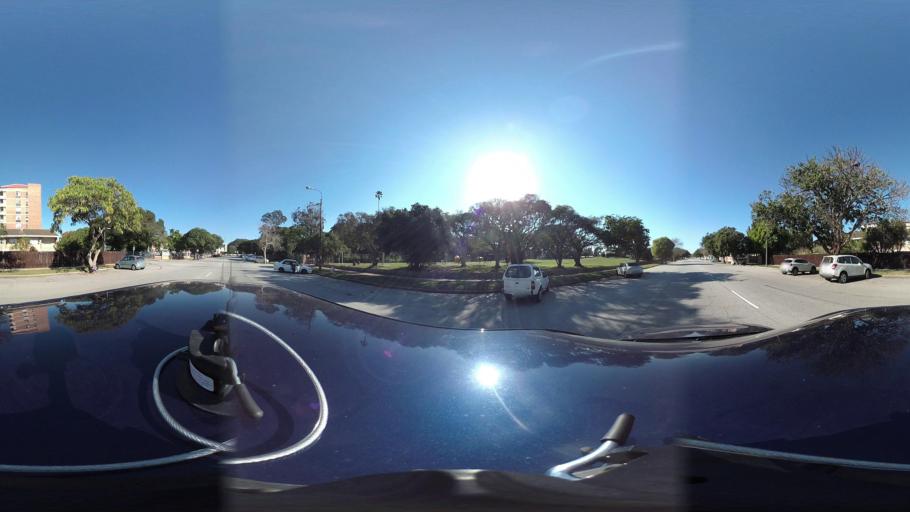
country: ZA
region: Eastern Cape
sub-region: Nelson Mandela Bay Metropolitan Municipality
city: Port Elizabeth
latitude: -33.9637
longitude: 25.6108
